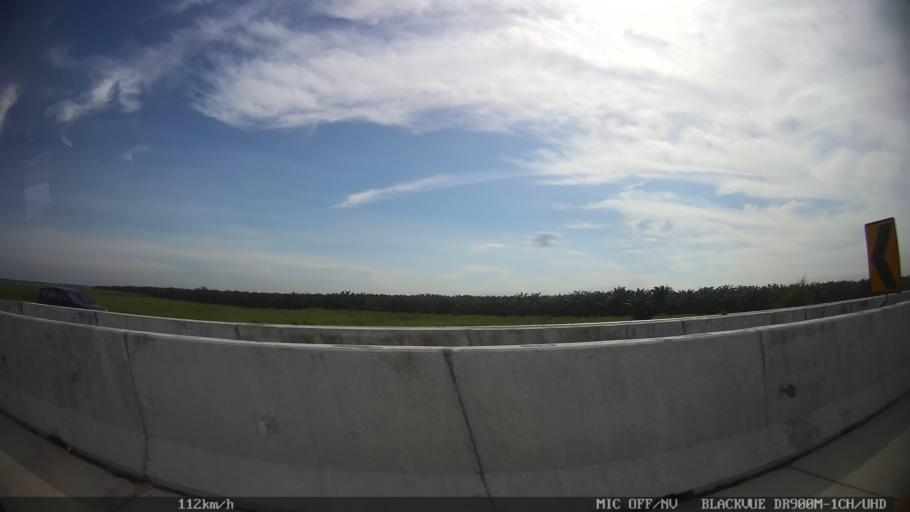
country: ID
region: North Sumatra
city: Binjai
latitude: 3.6527
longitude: 98.5368
